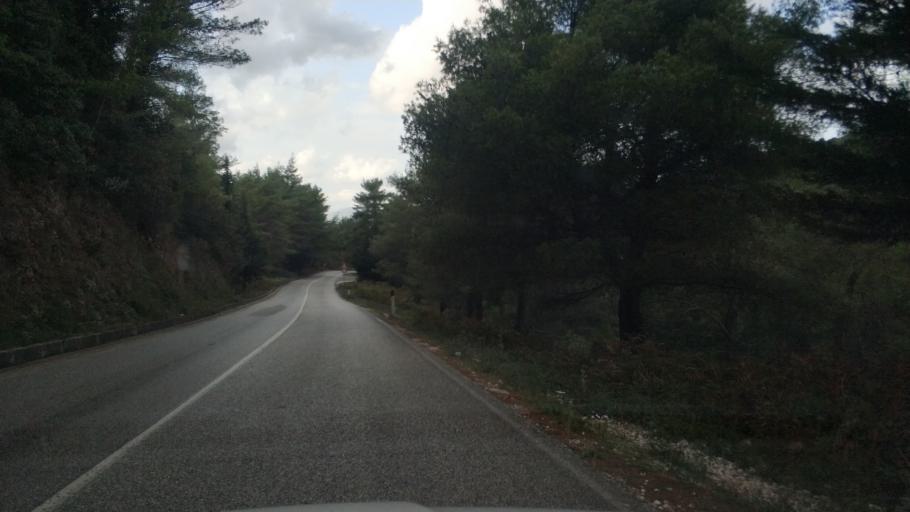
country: AL
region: Vlore
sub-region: Rrethi i Vlores
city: Orikum
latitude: 40.2520
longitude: 19.5385
